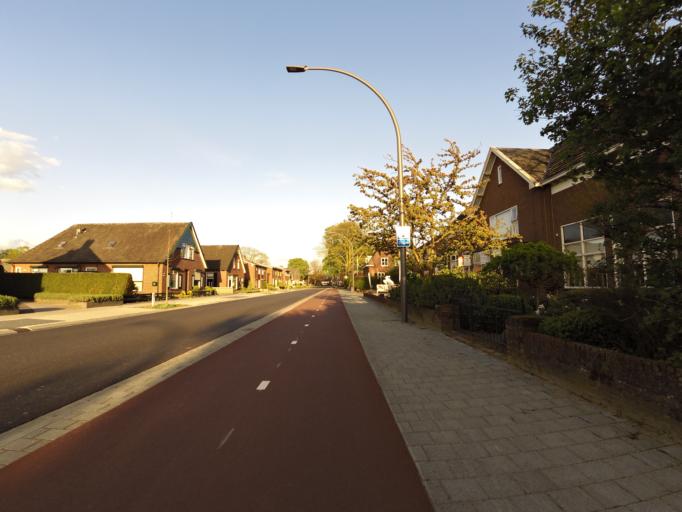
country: NL
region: Gelderland
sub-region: Oude IJsselstreek
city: Wisch
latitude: 51.9506
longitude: 6.4105
